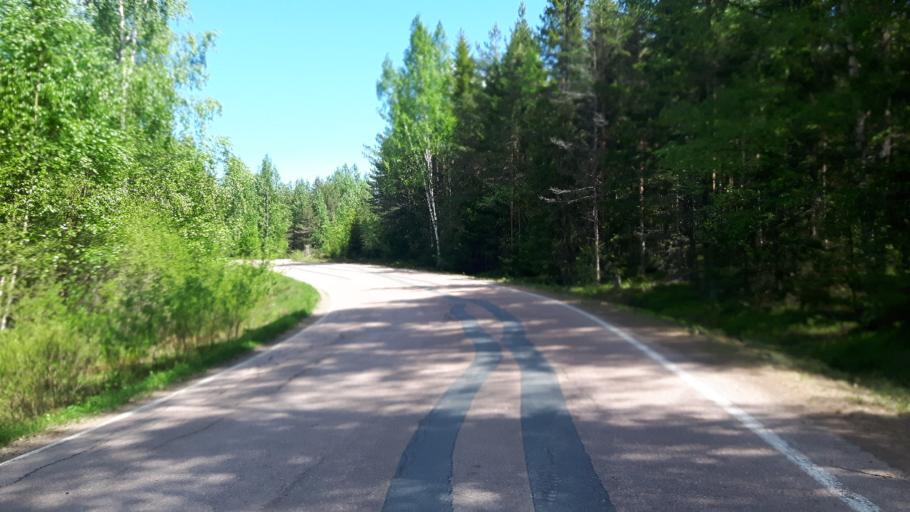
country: FI
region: Kymenlaakso
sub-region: Kotka-Hamina
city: Virolahti
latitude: 60.5468
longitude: 27.6460
